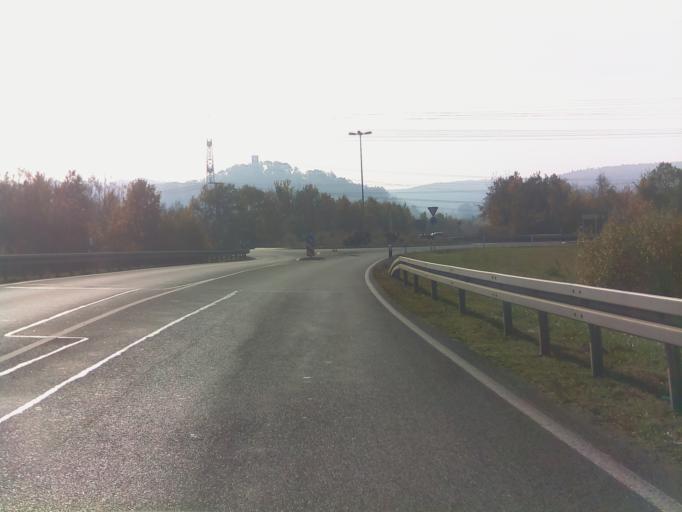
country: DE
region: Bavaria
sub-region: Regierungsbezirk Unterfranken
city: Ebelsbach
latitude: 49.9803
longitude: 10.6720
